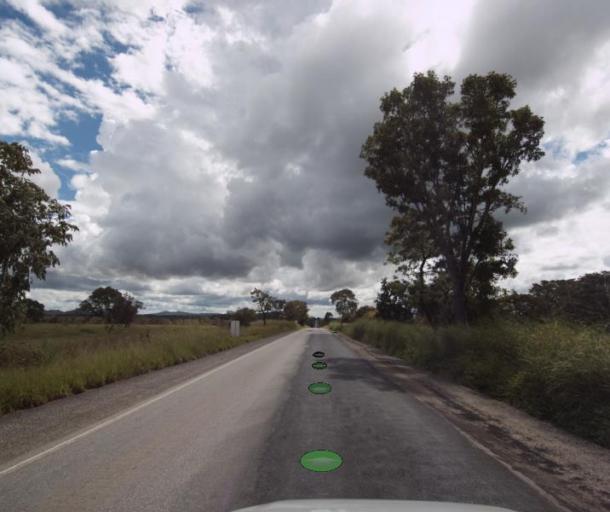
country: BR
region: Goias
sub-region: Uruacu
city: Uruacu
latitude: -14.2738
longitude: -49.1462
